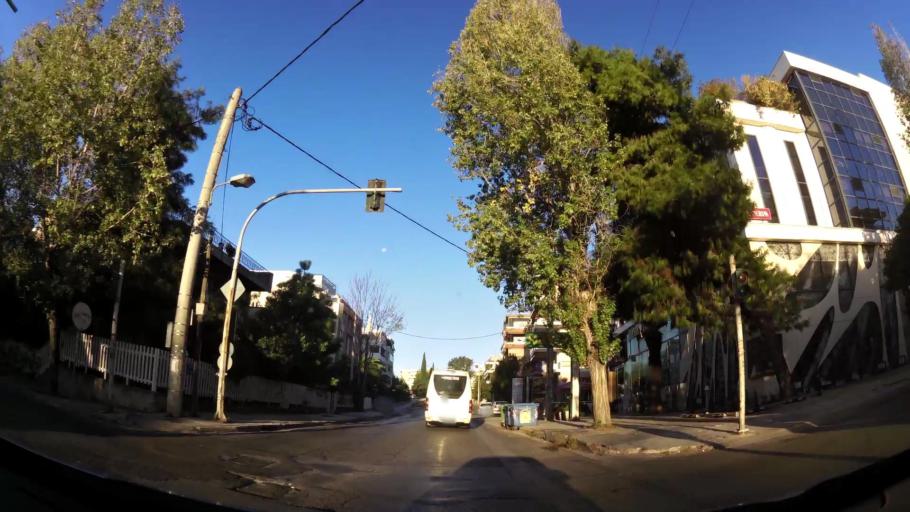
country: GR
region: Attica
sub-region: Nomarchia Athinas
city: Marousi
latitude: 38.0494
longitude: 23.7996
